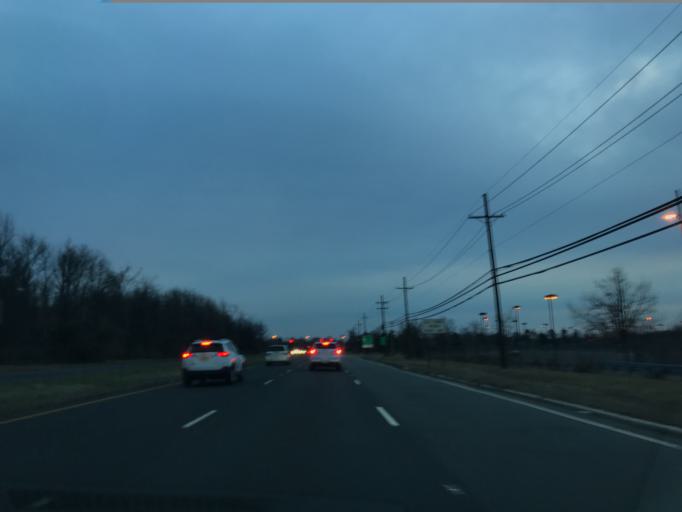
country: US
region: New Jersey
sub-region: Middlesex County
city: Dayton
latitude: 40.3500
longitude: -74.4971
